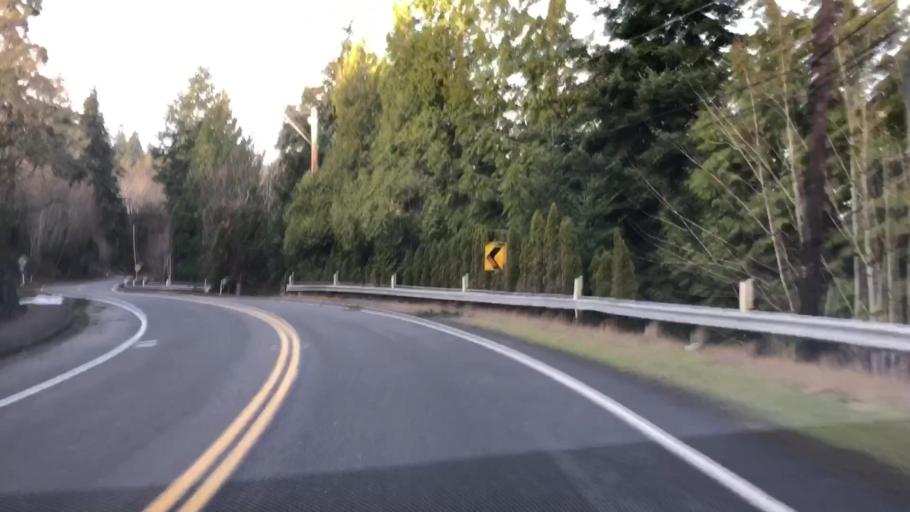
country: US
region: Washington
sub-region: King County
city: West Lake Sammamish
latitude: 47.5669
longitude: -122.1219
